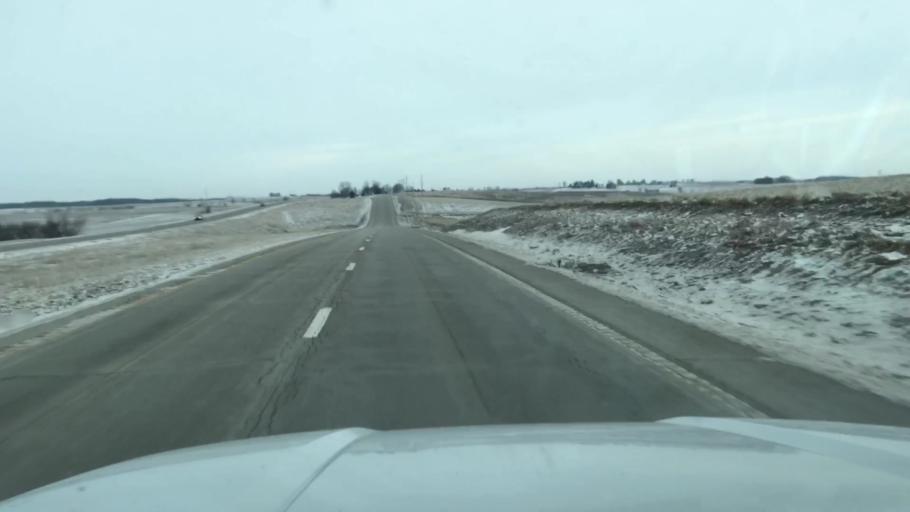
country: US
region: Missouri
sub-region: Andrew County
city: Savannah
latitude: 39.9772
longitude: -94.8766
